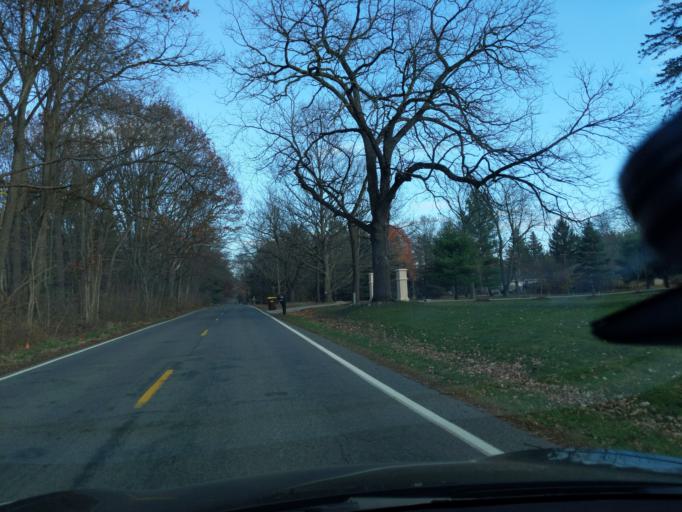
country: US
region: Michigan
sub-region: Ingham County
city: Haslett
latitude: 42.7152
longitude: -84.3599
